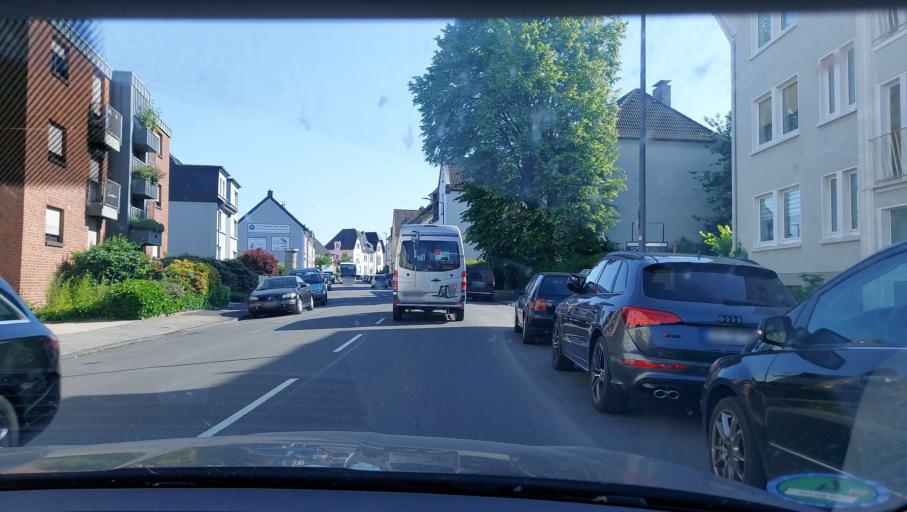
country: DE
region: North Rhine-Westphalia
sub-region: Regierungsbezirk Dusseldorf
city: Solingen
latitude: 51.1584
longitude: 7.0995
